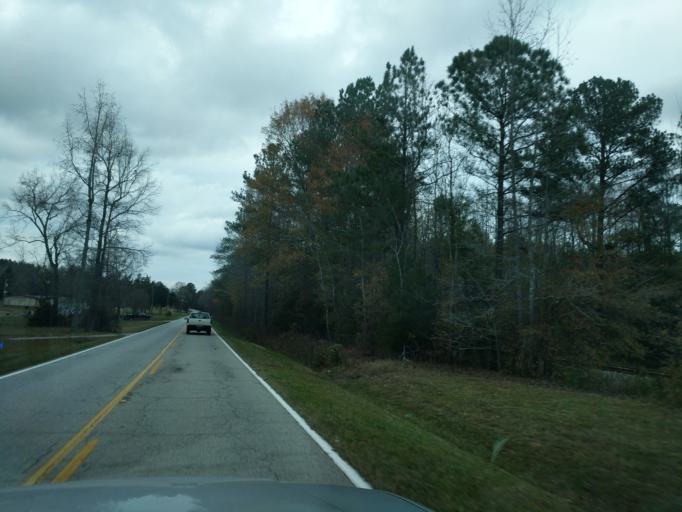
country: US
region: South Carolina
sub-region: Laurens County
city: Laurens
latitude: 34.4151
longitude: -82.0503
